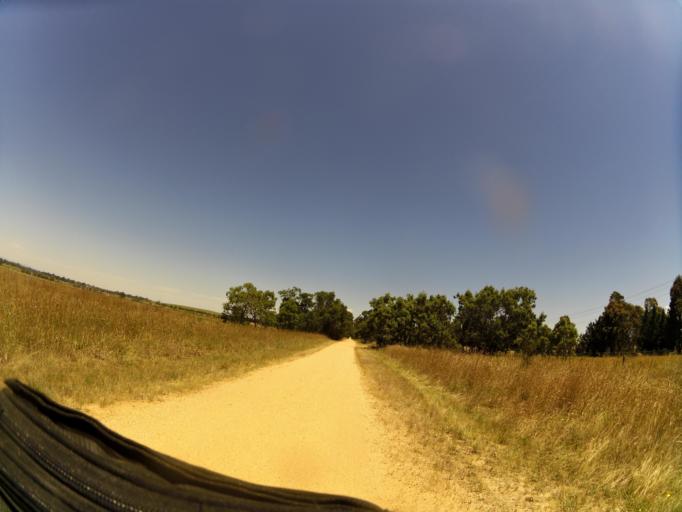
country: AU
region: Victoria
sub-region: Wellington
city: Sale
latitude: -37.9755
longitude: 147.0147
